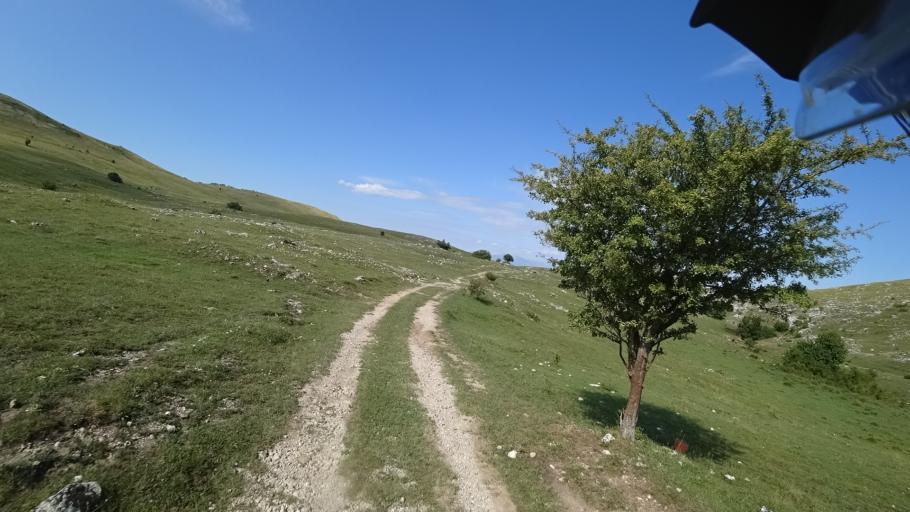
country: HR
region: Zadarska
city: Gracac
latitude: 44.2990
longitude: 15.9606
